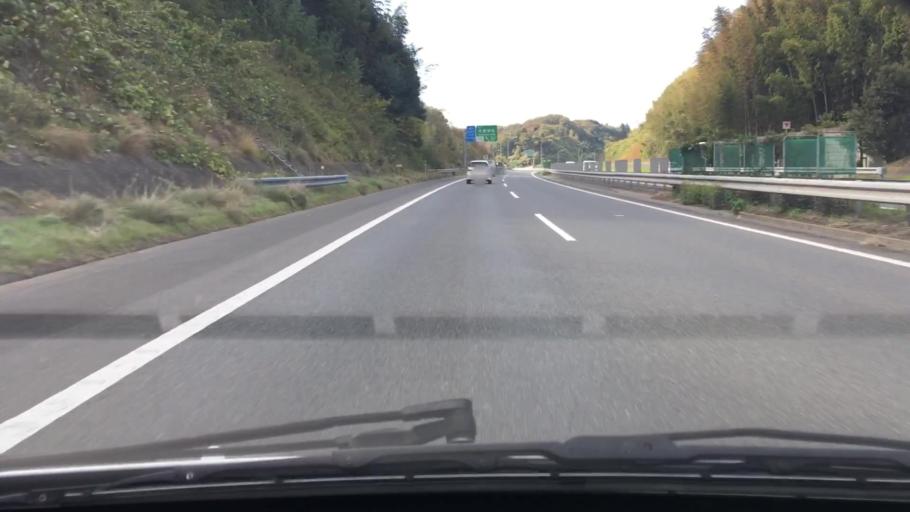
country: JP
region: Chiba
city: Kisarazu
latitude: 35.3890
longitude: 140.0012
